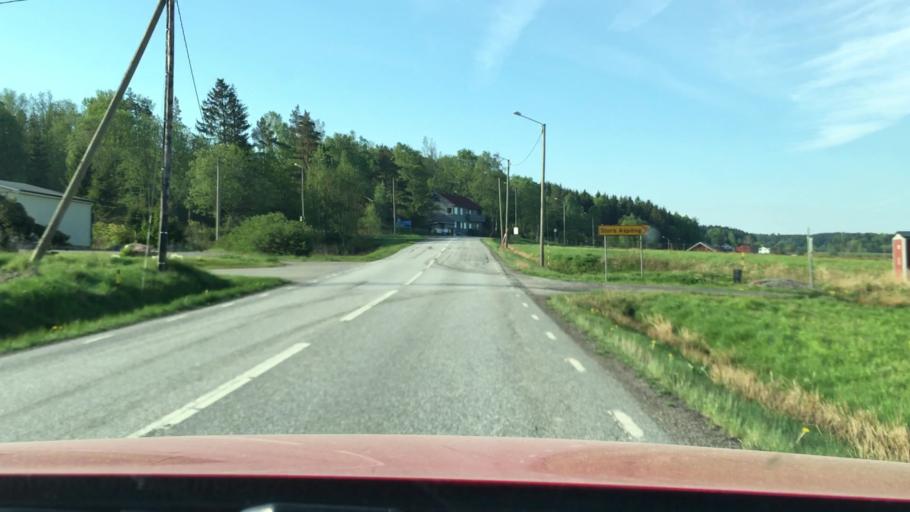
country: SE
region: Vaestra Goetaland
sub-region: Munkedals Kommun
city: Munkedal
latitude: 58.6063
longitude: 11.5590
